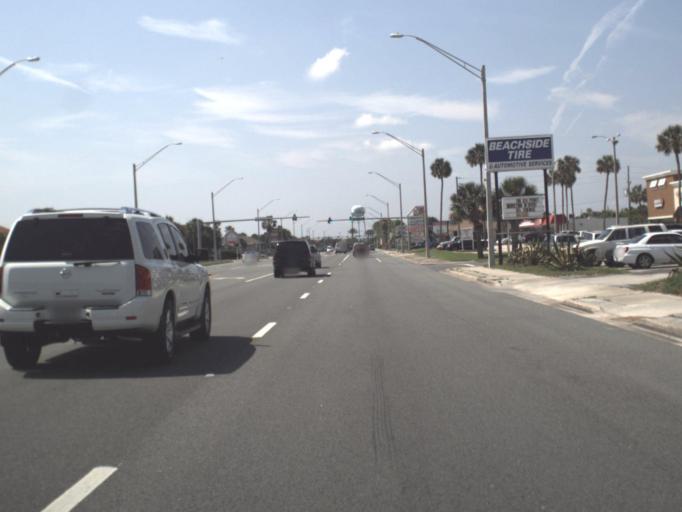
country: US
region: Florida
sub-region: Duval County
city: Jacksonville Beach
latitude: 30.2776
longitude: -81.3897
